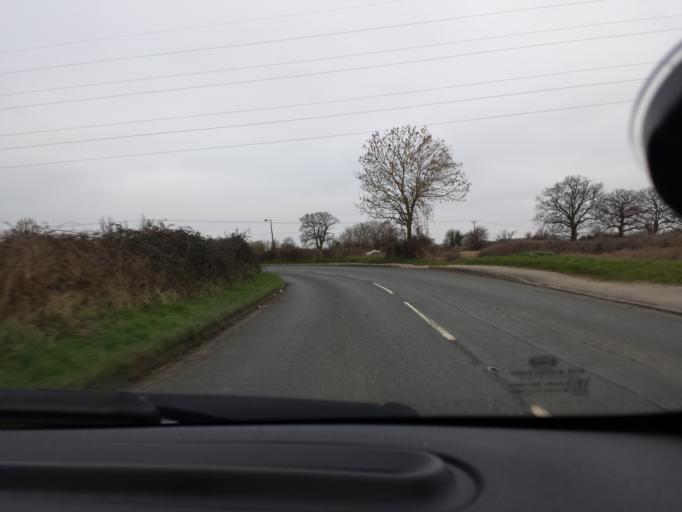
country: GB
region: England
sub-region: Wiltshire
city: Atworth
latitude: 51.3904
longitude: -2.1730
